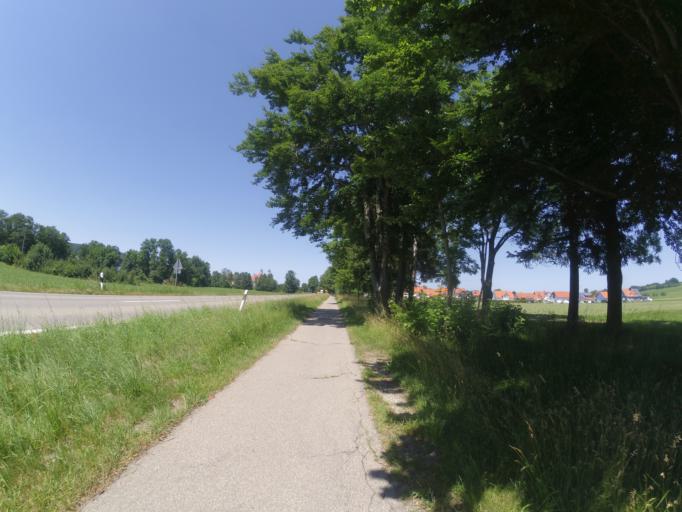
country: DE
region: Bavaria
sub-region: Swabia
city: Ottobeuren
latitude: 47.9321
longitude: 10.3055
